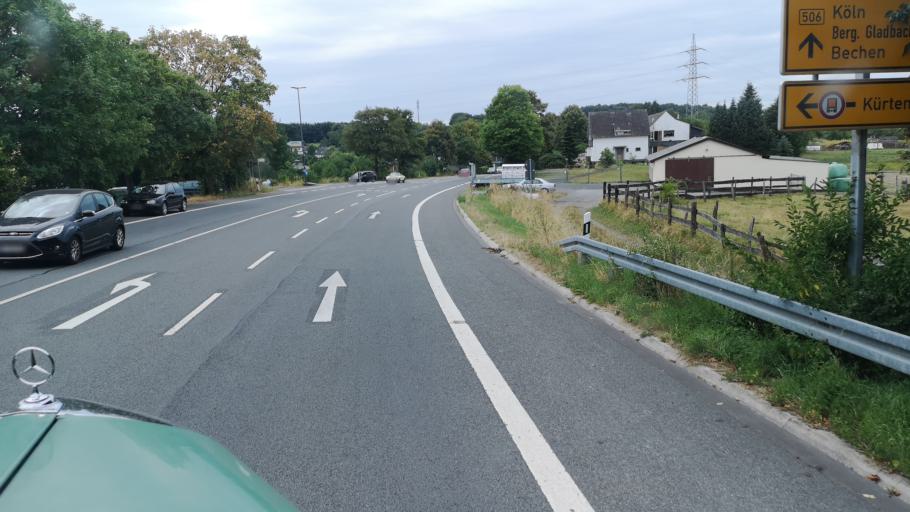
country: DE
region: North Rhine-Westphalia
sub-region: Regierungsbezirk Koln
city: Kurten
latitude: 51.0606
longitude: 7.2359
